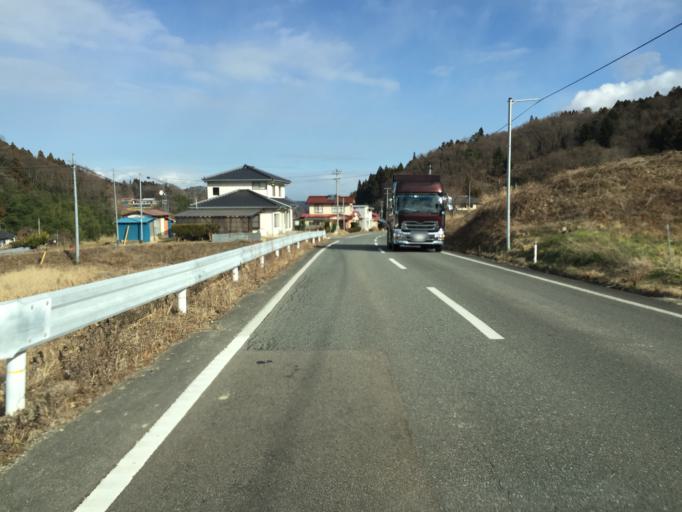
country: JP
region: Fukushima
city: Fukushima-shi
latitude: 37.7255
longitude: 140.5508
